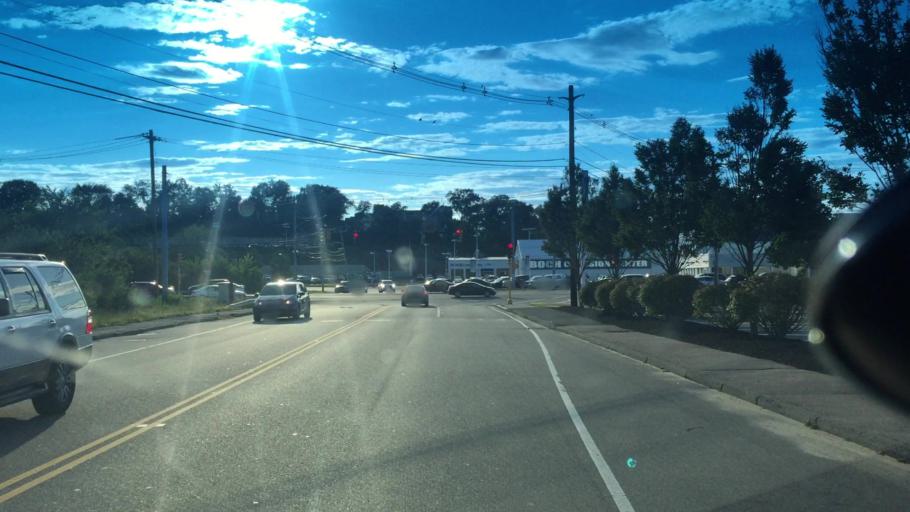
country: US
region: Massachusetts
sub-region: Norfolk County
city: Norwood
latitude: 42.1708
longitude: -71.1951
